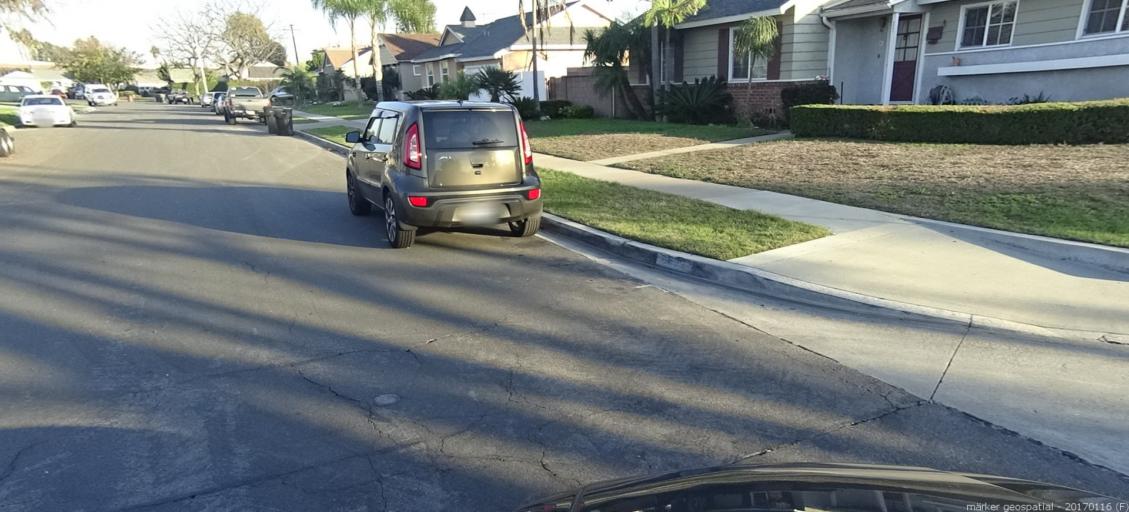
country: US
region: California
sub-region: Orange County
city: Stanton
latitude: 33.8039
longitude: -117.9794
